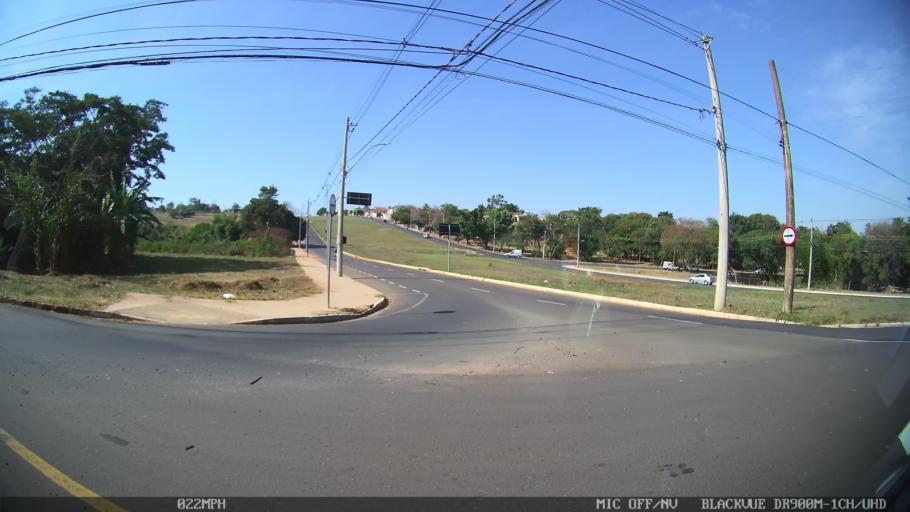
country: BR
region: Sao Paulo
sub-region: Sao Jose Do Rio Preto
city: Sao Jose do Rio Preto
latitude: -20.7936
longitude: -49.4255
